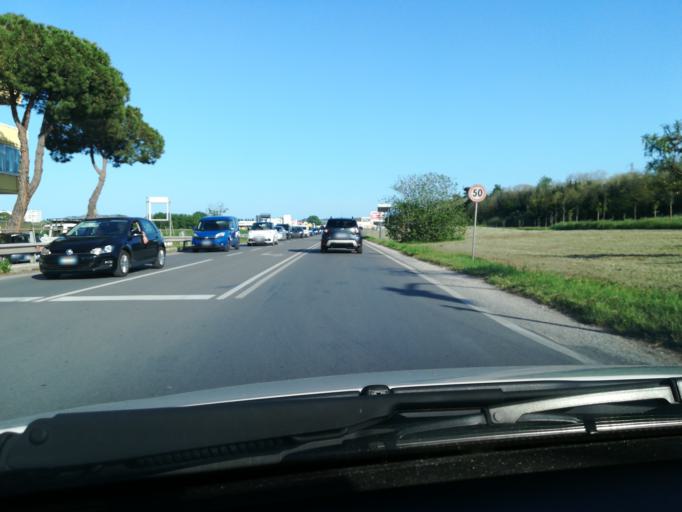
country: IT
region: Emilia-Romagna
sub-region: Provincia di Rimini
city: Misano Adriatico
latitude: 43.9738
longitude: 12.6963
